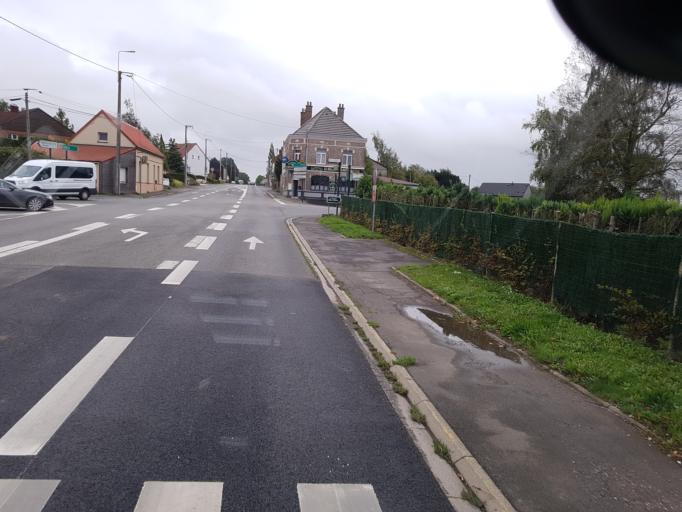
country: FR
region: Nord-Pas-de-Calais
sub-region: Departement du Pas-de-Calais
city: Neuville-Saint-Vaast
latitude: 50.3513
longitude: 2.7492
